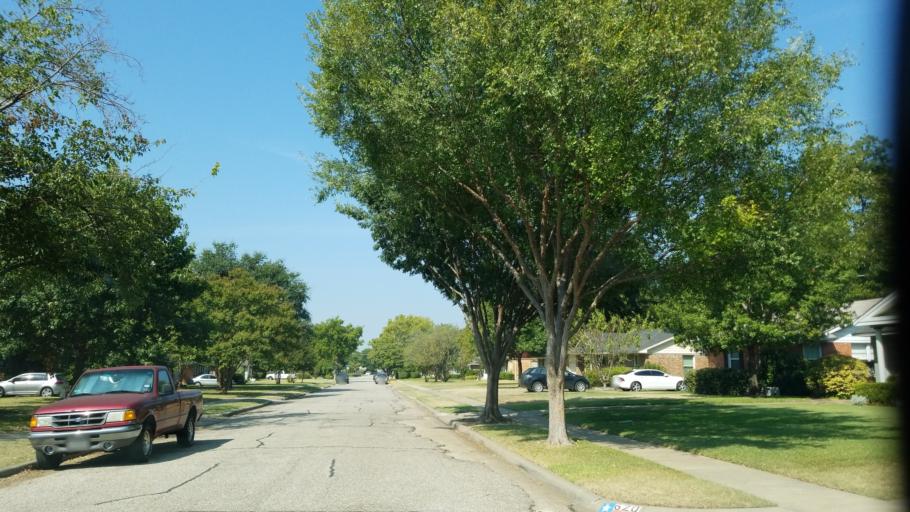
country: US
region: Texas
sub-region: Dallas County
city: Richardson
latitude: 32.9537
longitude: -96.7417
